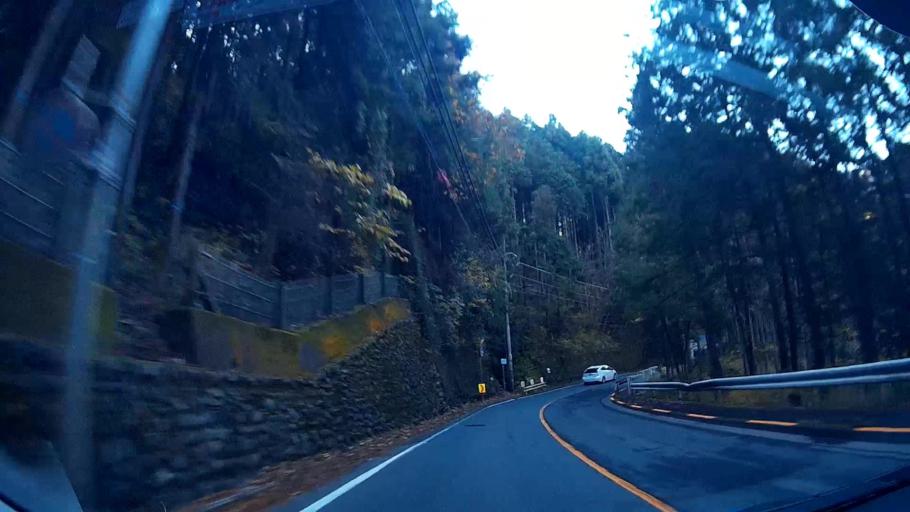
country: JP
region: Tokyo
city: Itsukaichi
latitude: 35.7232
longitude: 139.1690
